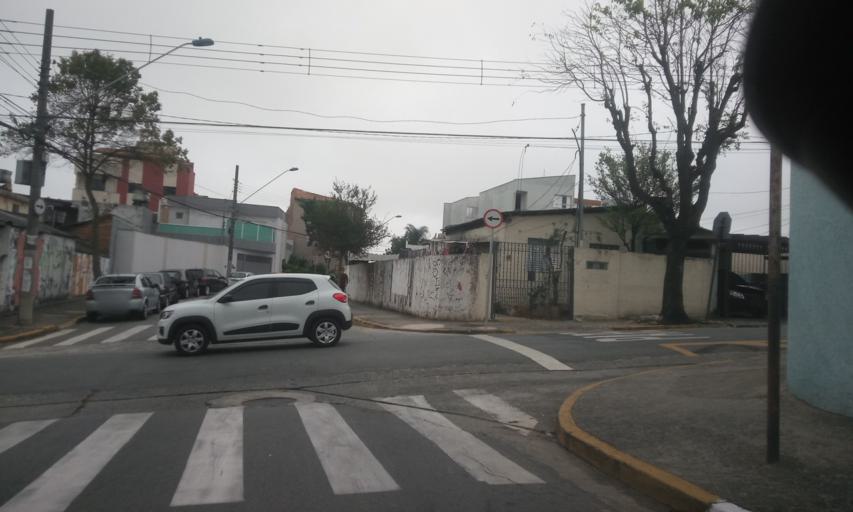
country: BR
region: Sao Paulo
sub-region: Sao Caetano Do Sul
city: Sao Caetano do Sul
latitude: -23.6379
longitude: -46.5693
